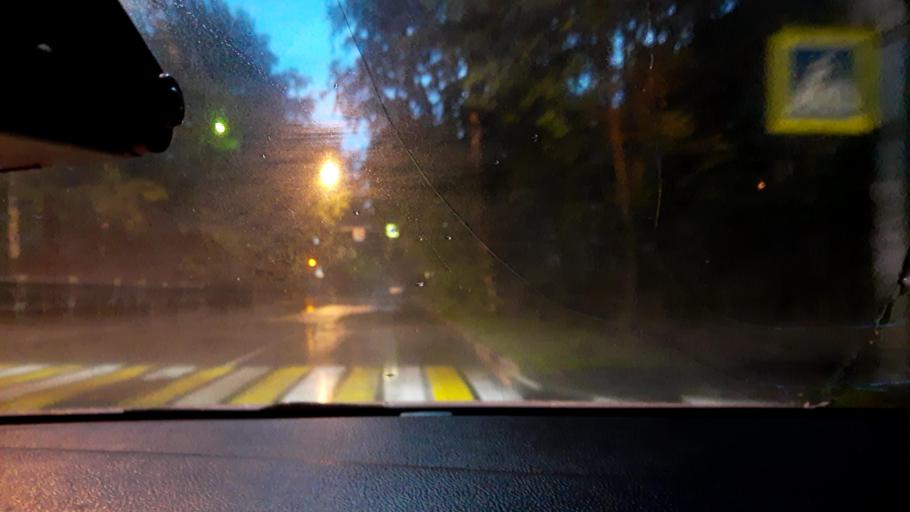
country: RU
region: Moskovskaya
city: Krasnogorsk
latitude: 55.8158
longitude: 37.3341
